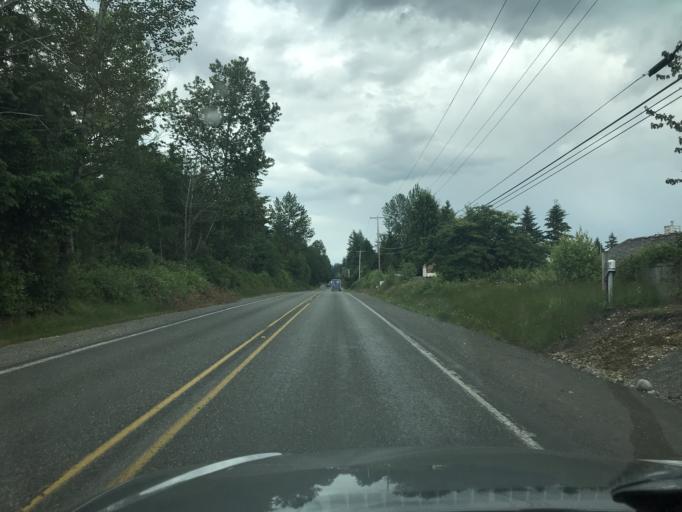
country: US
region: Washington
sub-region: Pierce County
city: Prairie Ridge
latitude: 47.1475
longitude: -122.1622
